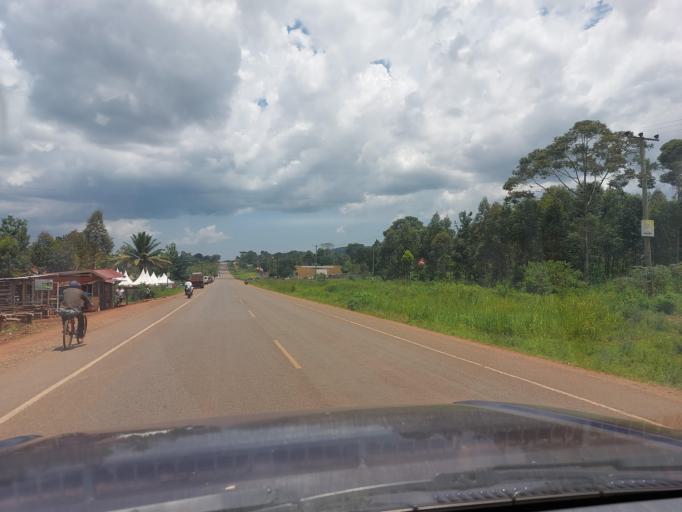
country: UG
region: Central Region
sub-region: Mukono District
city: Mukono
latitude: 0.2931
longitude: 32.7858
